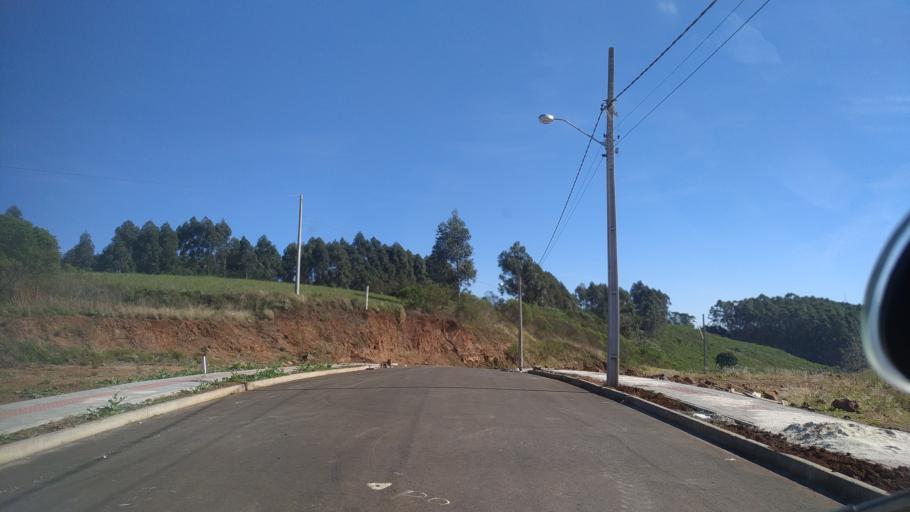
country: BR
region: Santa Catarina
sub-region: Chapeco
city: Chapeco
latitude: -27.0480
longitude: -52.6041
